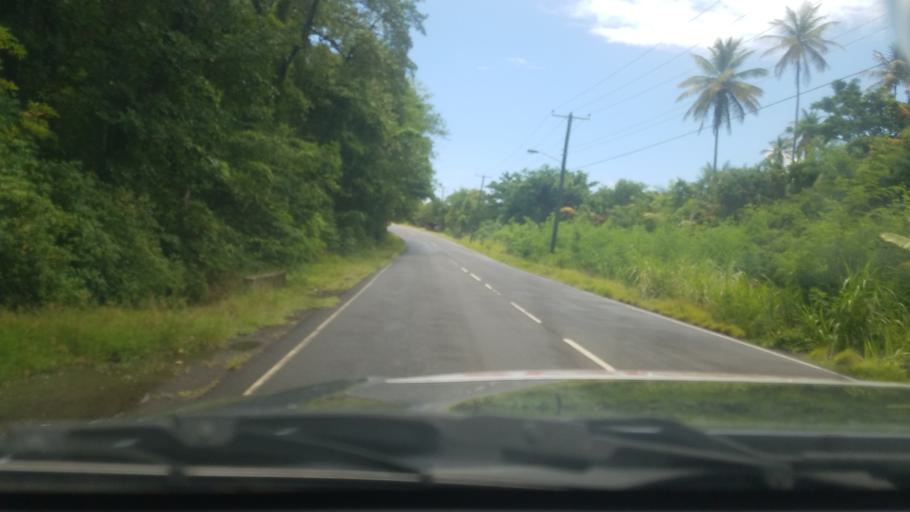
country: LC
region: Praslin
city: Praslin
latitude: 13.8798
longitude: -60.8970
